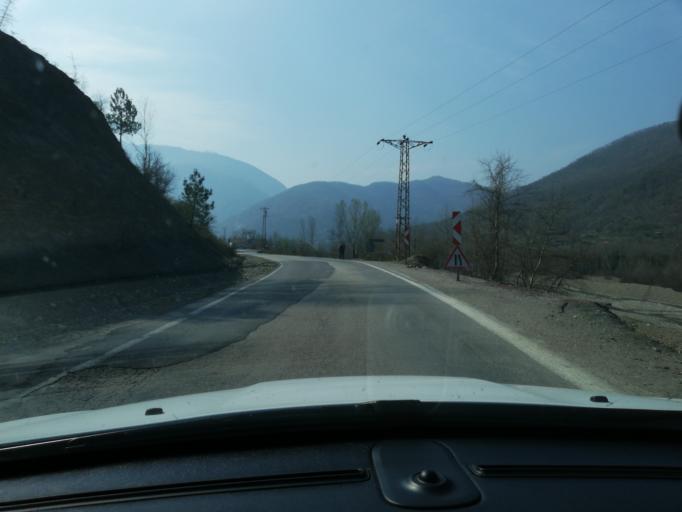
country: TR
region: Karabuk
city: Yenice
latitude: 41.2231
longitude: 32.3622
